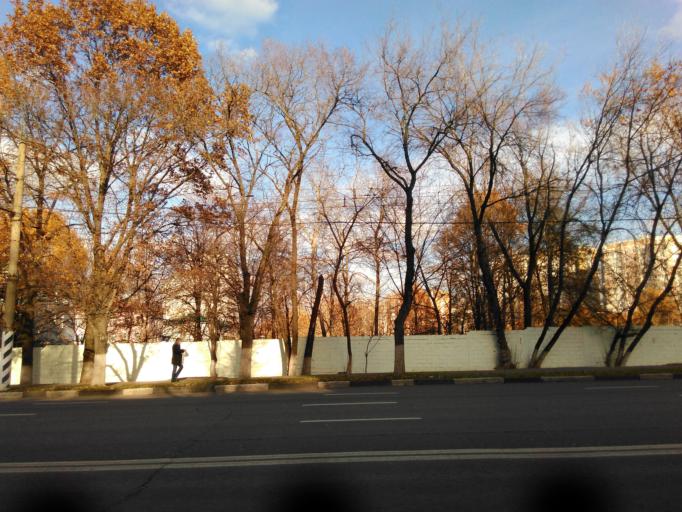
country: RU
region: Moscow
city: Zyuzino
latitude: 55.6526
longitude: 37.5826
